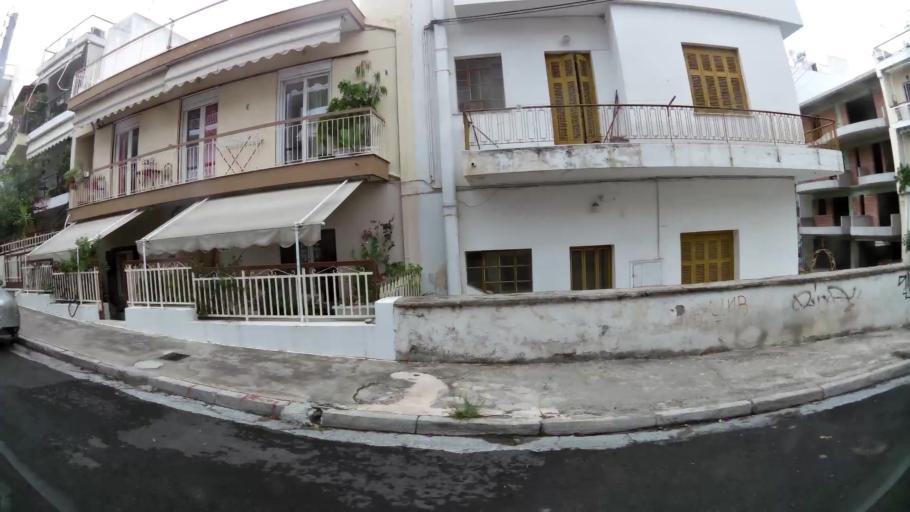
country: GR
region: Attica
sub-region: Nomarchia Athinas
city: Kaisariani
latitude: 37.9521
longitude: 23.7617
